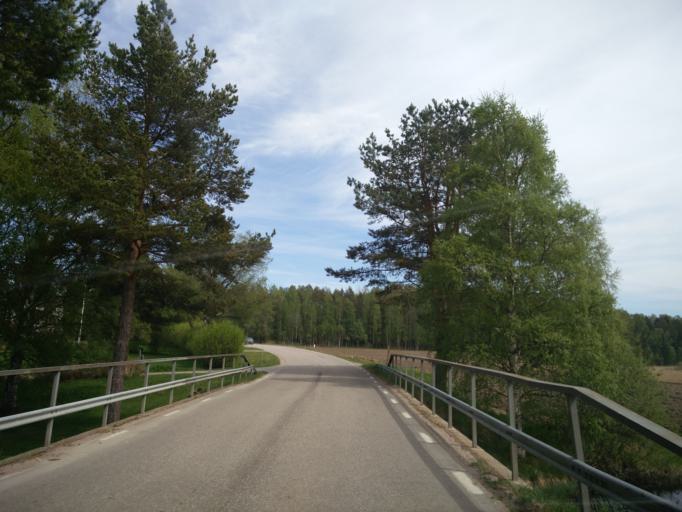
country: SE
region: Gaevleborg
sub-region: Hudiksvalls Kommun
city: Sorforsa
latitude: 61.6941
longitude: 16.9286
